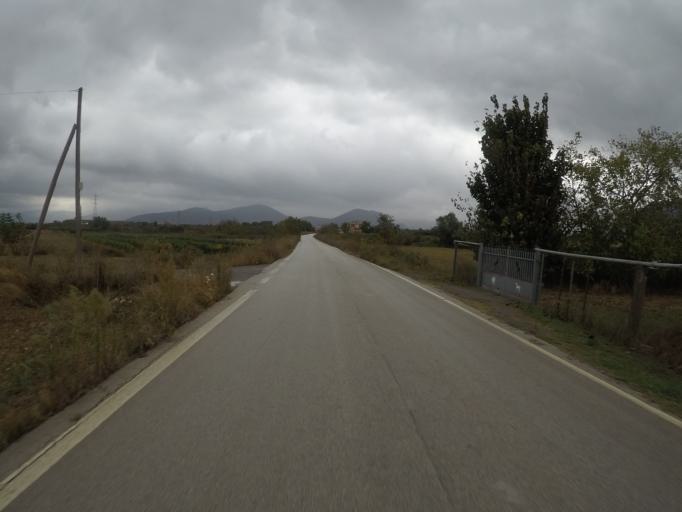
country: GR
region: Peloponnese
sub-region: Nomos Arkadias
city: Tripoli
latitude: 37.5653
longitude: 22.4066
